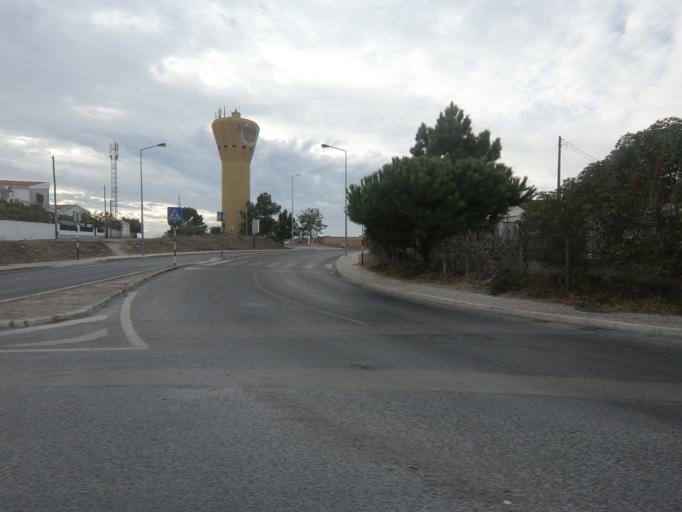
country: PT
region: Setubal
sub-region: Almada
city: Charneca
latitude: 38.6234
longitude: -9.1990
